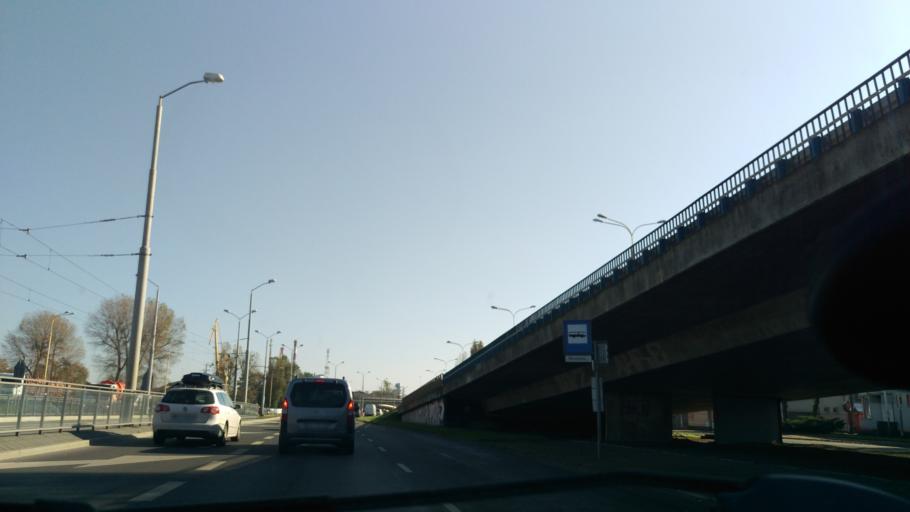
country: PL
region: West Pomeranian Voivodeship
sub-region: Szczecin
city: Szczecin
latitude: 53.4150
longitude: 14.5700
